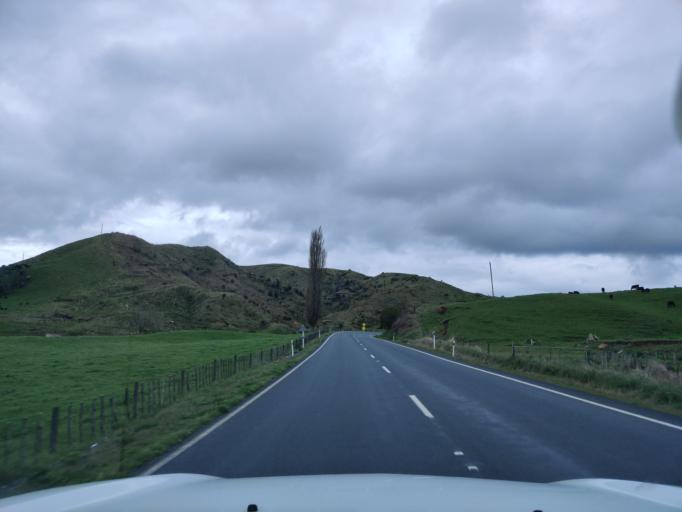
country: NZ
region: Waikato
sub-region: Otorohanga District
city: Otorohanga
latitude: -38.5191
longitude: 175.1952
